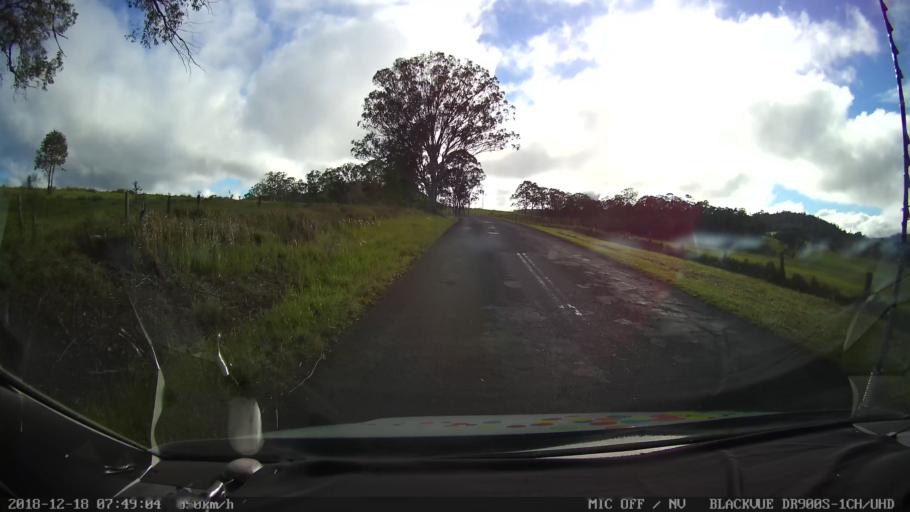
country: AU
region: New South Wales
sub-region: Kyogle
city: Kyogle
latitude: -28.4562
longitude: 152.5681
